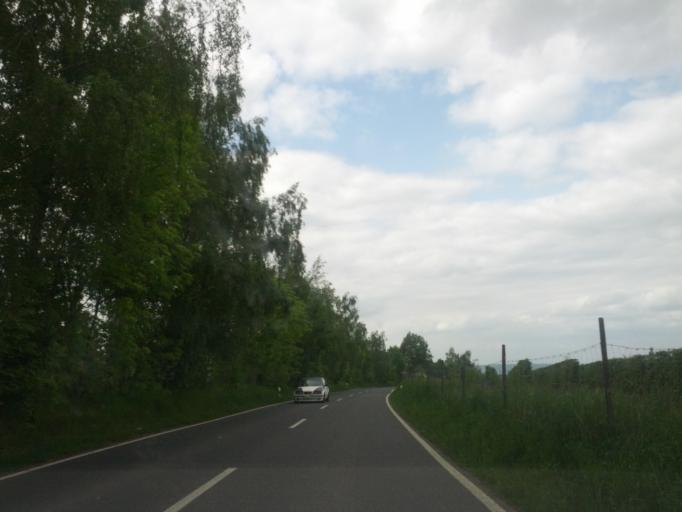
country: DE
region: Saxony
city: Kreischa
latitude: 50.9514
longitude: 13.7949
